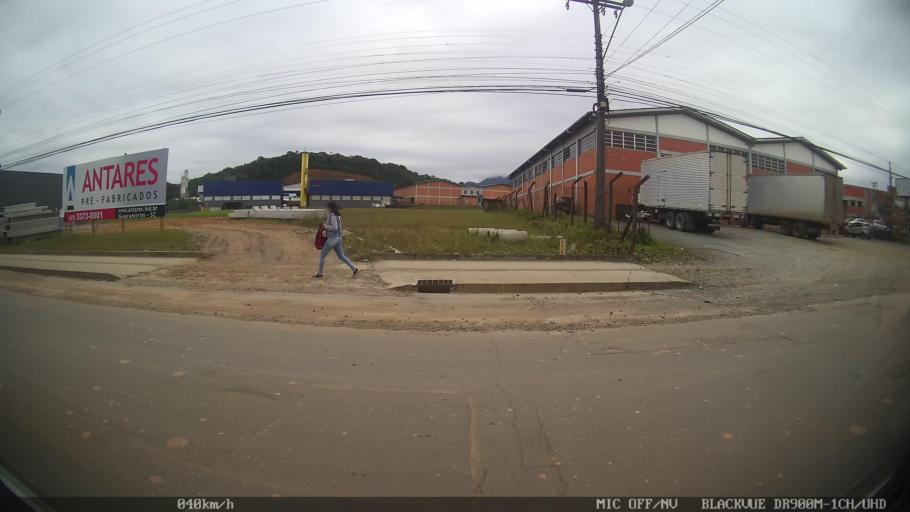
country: BR
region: Santa Catarina
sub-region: Joinville
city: Joinville
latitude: -26.2608
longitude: -48.8836
